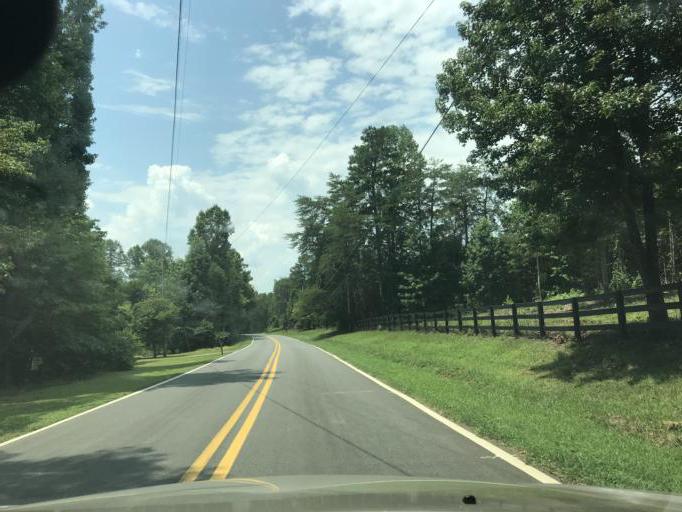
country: US
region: Georgia
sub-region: Dawson County
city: Dawsonville
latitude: 34.3335
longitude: -84.1936
